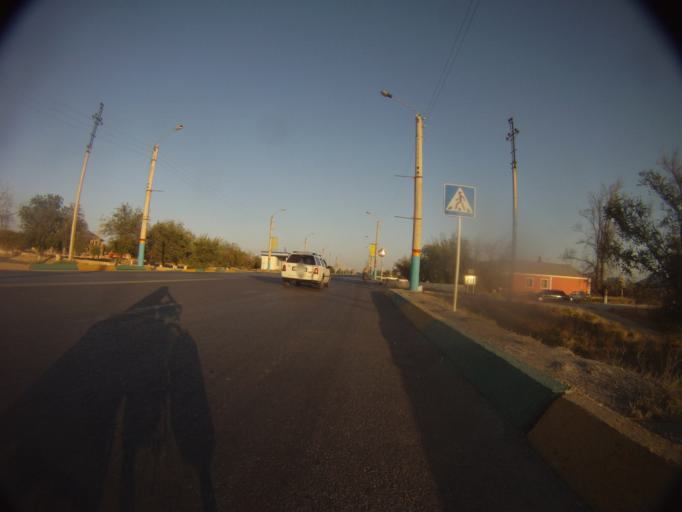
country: KZ
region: Ongtustik Qazaqstan
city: Turkestan
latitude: 43.2933
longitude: 68.2882
